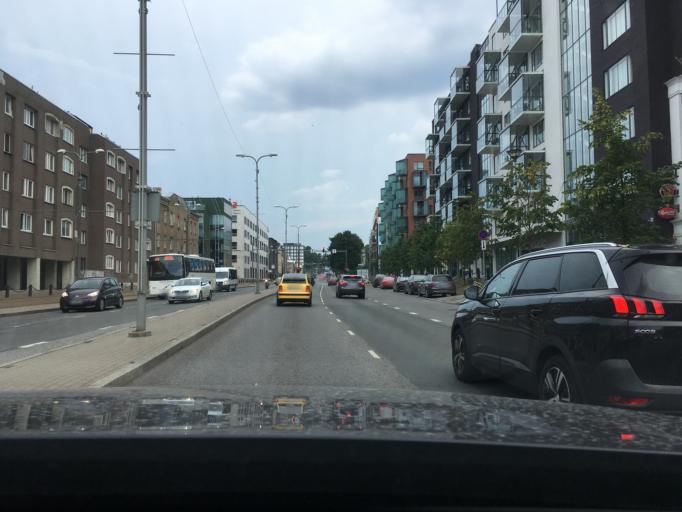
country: EE
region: Harju
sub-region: Tallinna linn
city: Tallinn
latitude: 59.4306
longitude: 24.7708
